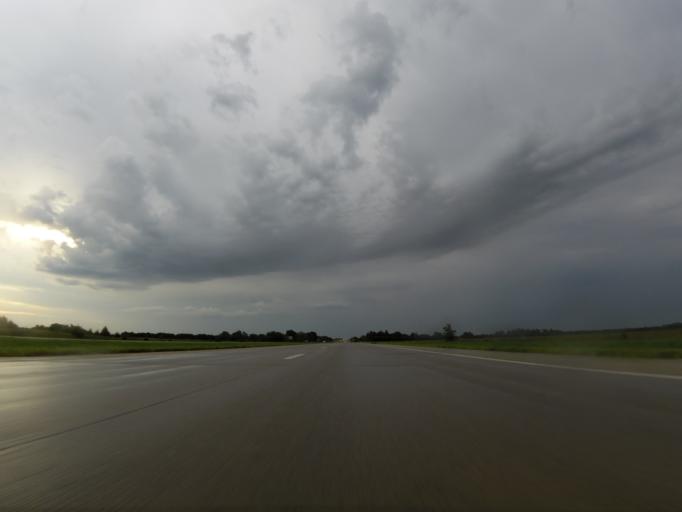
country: US
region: Kansas
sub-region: Reno County
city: Haven
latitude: 37.9319
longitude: -97.8545
